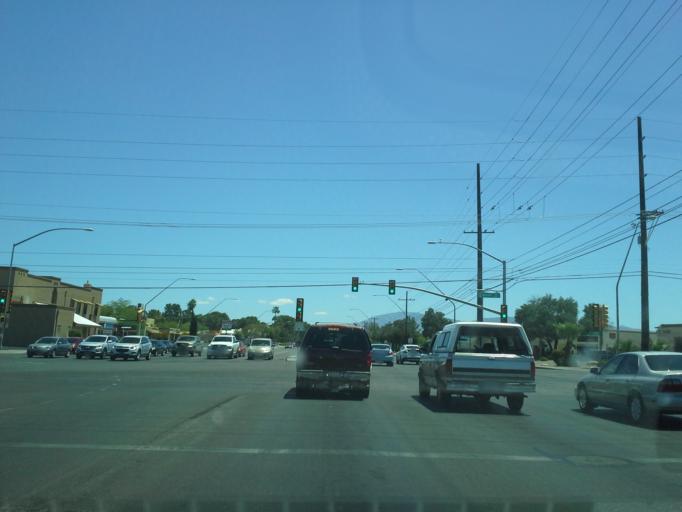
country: US
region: Arizona
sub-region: Pima County
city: Tucson
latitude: 32.2506
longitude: -110.8757
